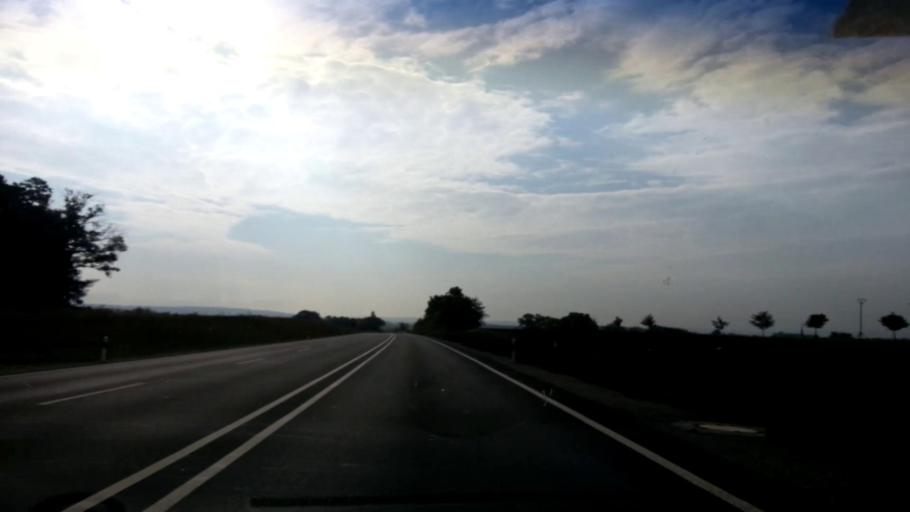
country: DE
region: Bavaria
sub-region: Regierungsbezirk Unterfranken
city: Gerolzhofen
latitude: 49.8798
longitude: 10.3579
